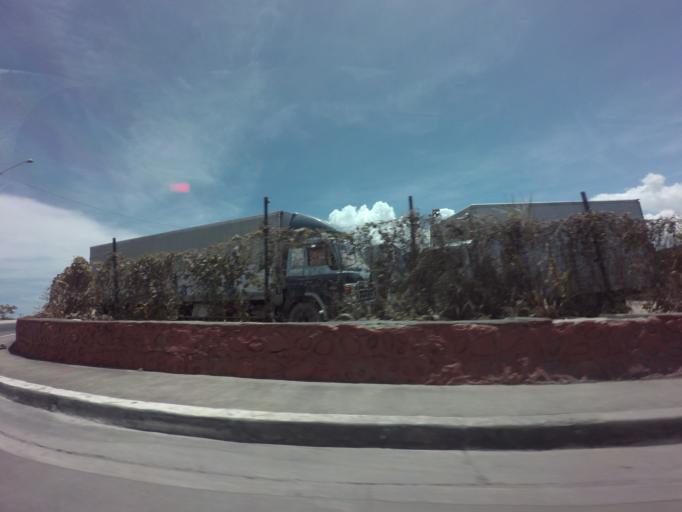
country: PH
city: Sambayanihan People's Village
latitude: 14.4919
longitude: 120.9965
